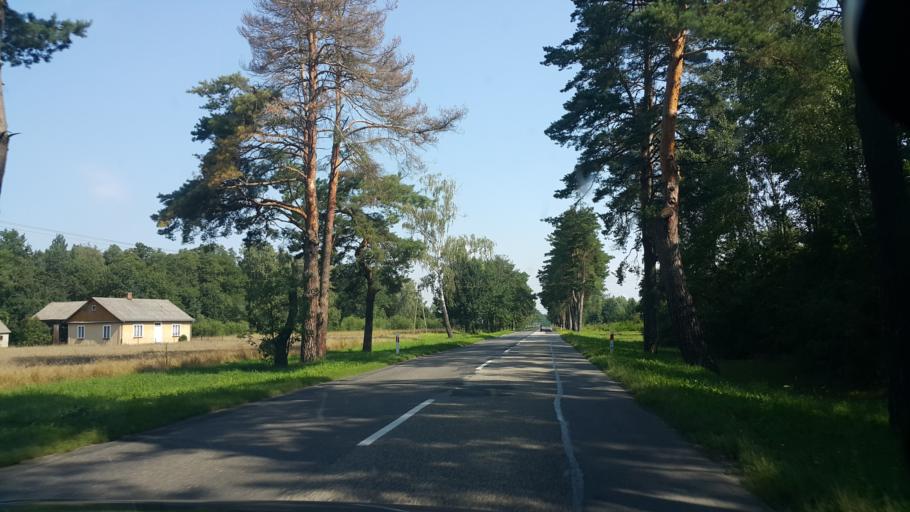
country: PL
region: Lublin Voivodeship
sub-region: Powiat leczynski
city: Cycow
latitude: 51.3405
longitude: 23.1564
